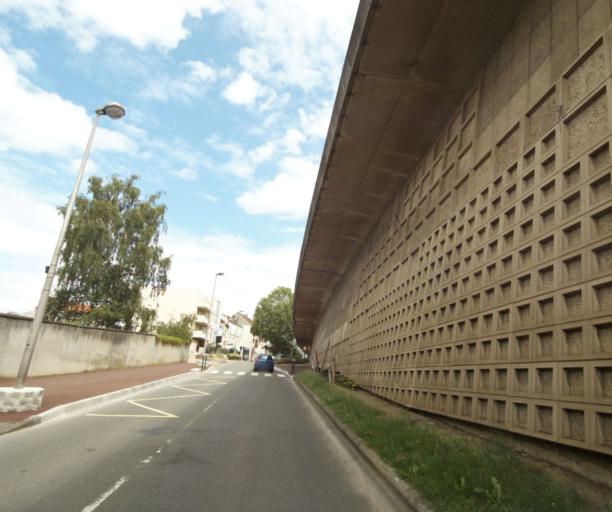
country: FR
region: Ile-de-France
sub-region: Departement des Yvelines
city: Saint-Cyr-l'Ecole
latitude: 48.7988
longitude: 2.0710
